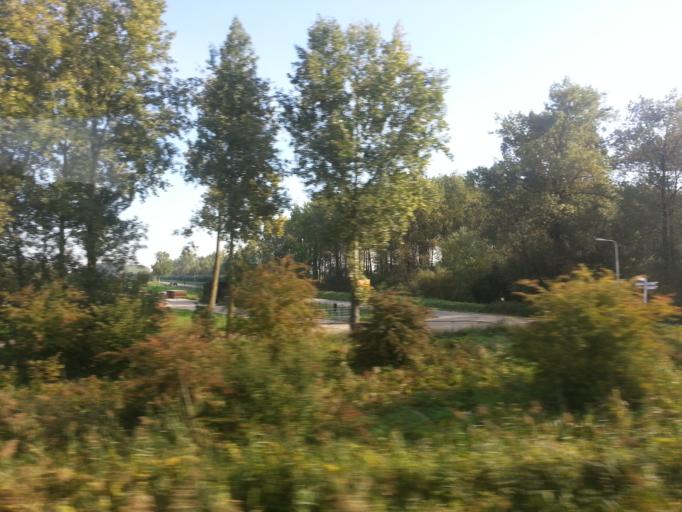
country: NL
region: Gelderland
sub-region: Gemeente Culemborg
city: Culemborg
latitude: 51.9276
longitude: 5.2430
